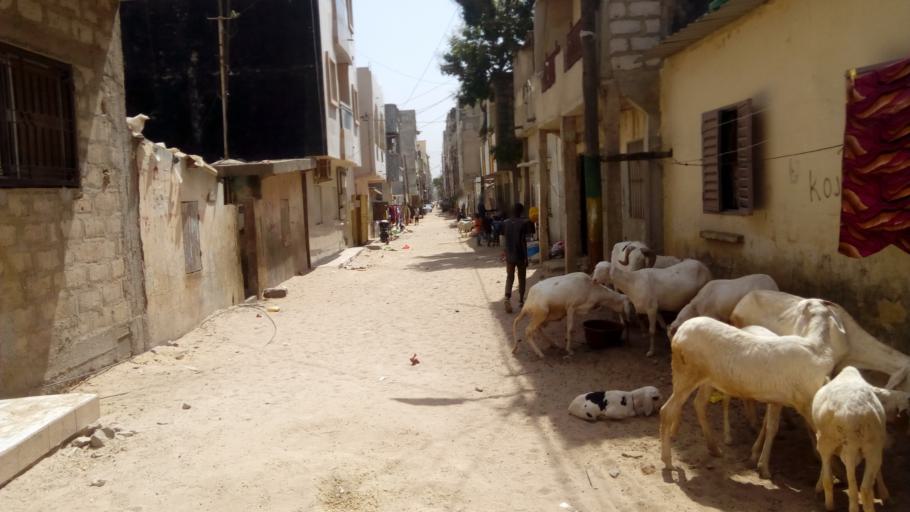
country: SN
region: Dakar
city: Grand Dakar
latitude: 14.7152
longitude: -17.4489
